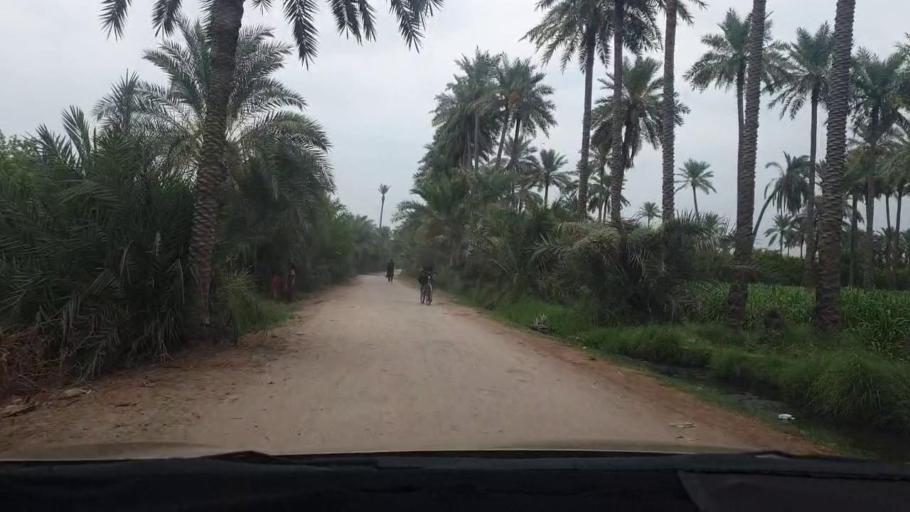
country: PK
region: Sindh
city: Larkana
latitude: 27.5644
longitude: 68.2302
